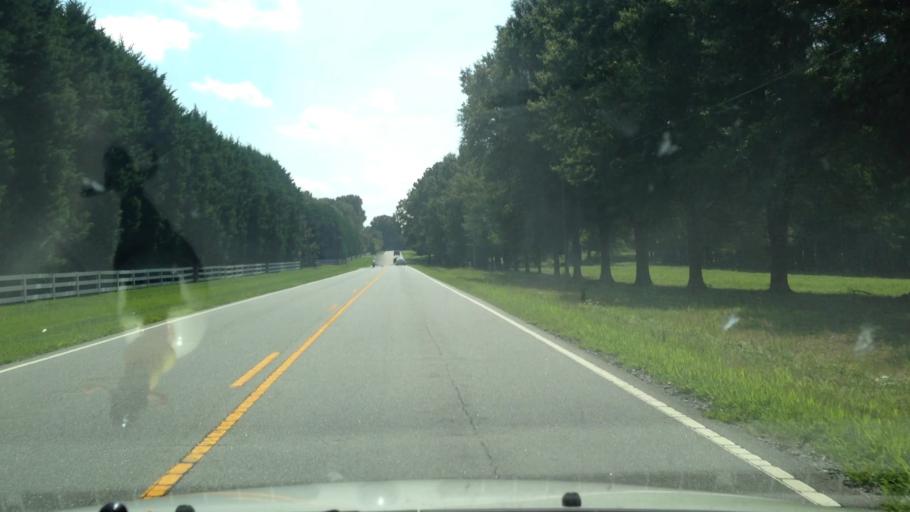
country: US
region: North Carolina
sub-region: Guilford County
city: Oak Ridge
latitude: 36.1672
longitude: -79.9982
